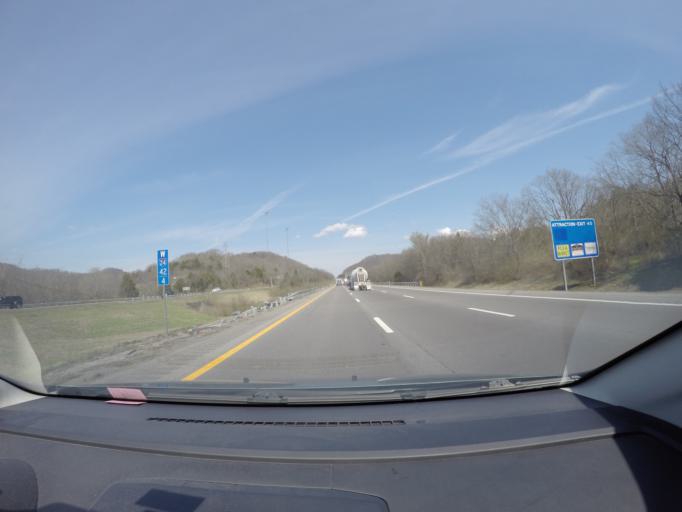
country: US
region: Tennessee
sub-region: Davidson County
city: Nashville
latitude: 36.2523
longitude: -86.7847
